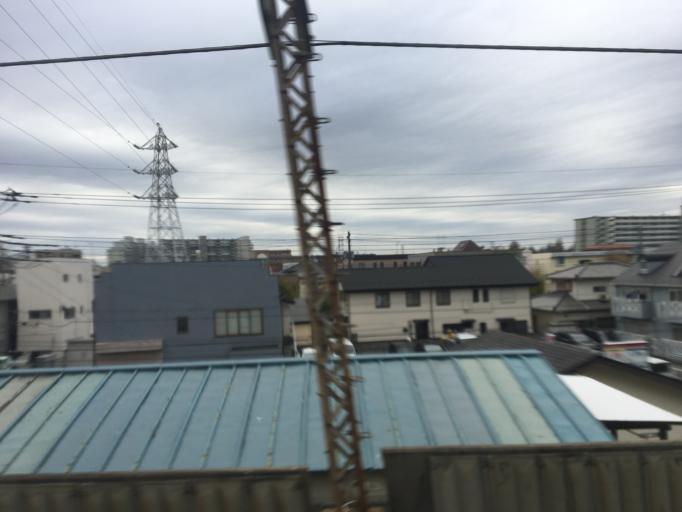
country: JP
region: Chiba
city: Nagareyama
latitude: 35.8286
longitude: 139.9150
